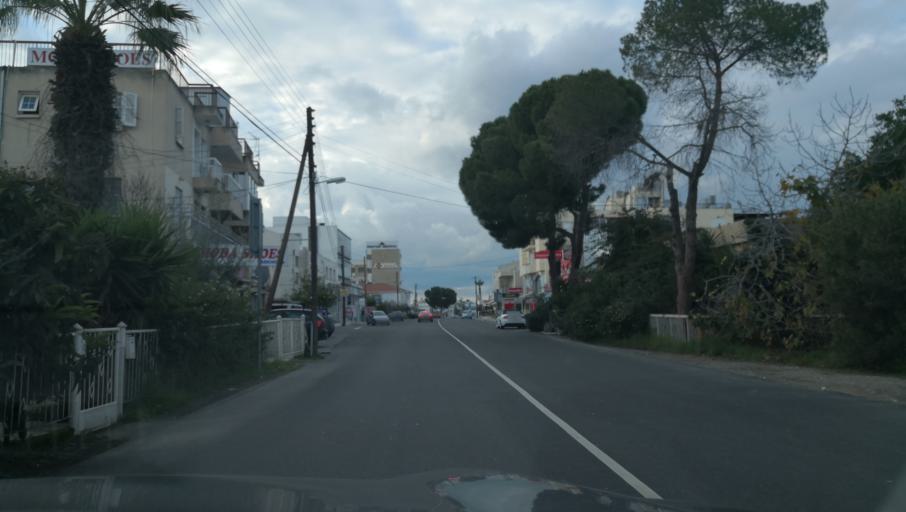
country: CY
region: Lefkosia
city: Nicosia
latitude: 35.1372
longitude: 33.3504
